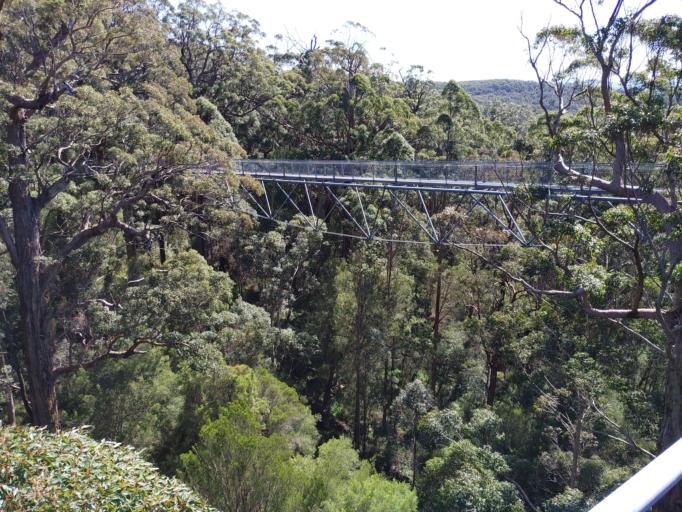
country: AU
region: Western Australia
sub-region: Denmark
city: Denmark
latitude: -34.9758
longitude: 116.8950
